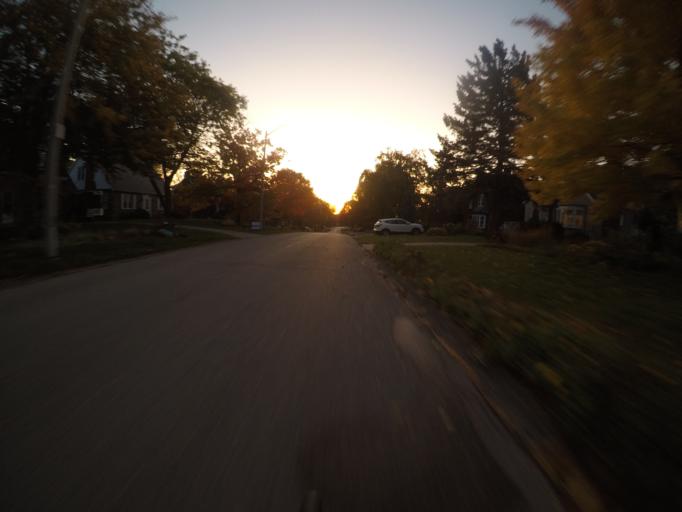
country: CA
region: Ontario
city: Kitchener
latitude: 43.4378
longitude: -80.4650
